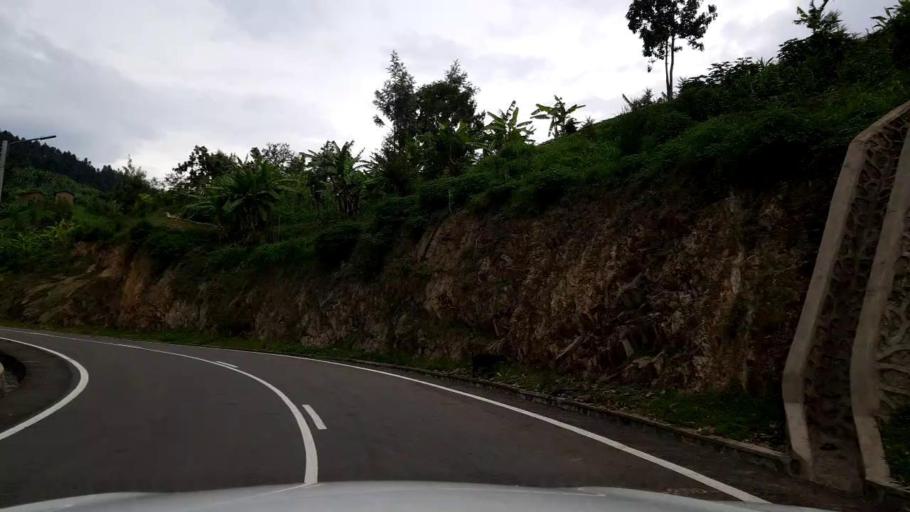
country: RW
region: Western Province
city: Kibuye
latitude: -2.0282
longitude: 29.3952
